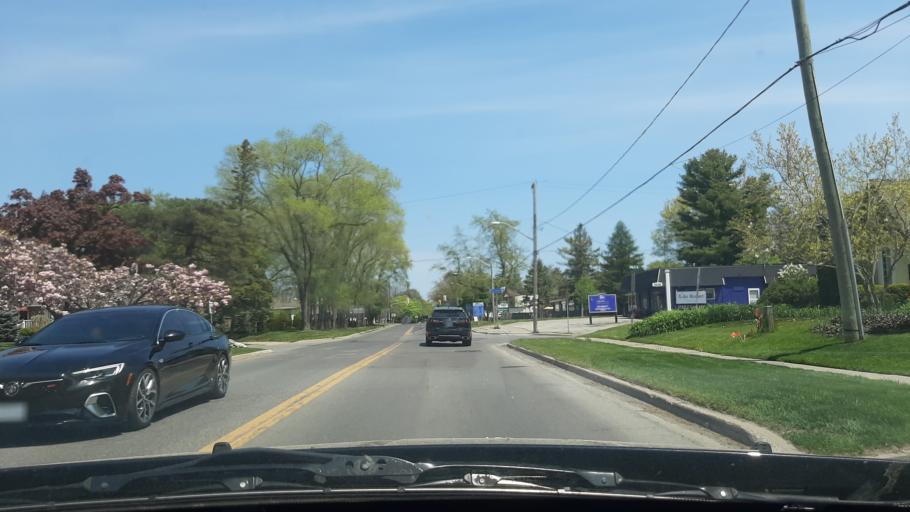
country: US
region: New York
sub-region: Niagara County
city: Youngstown
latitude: 43.2515
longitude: -79.0851
